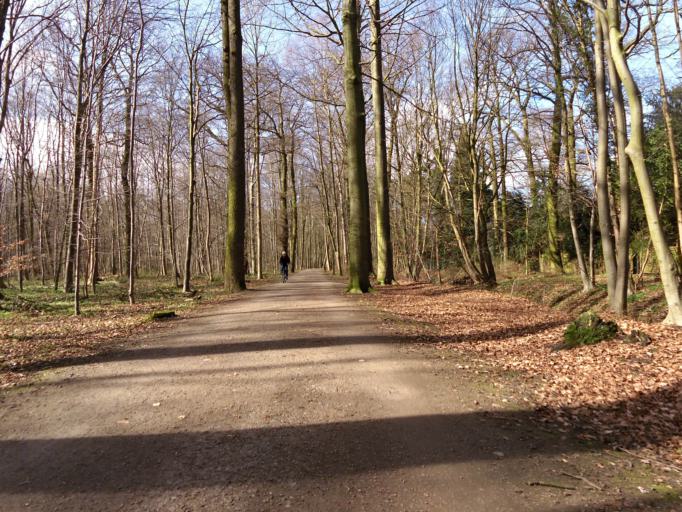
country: DE
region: Lower Saxony
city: Laatzen
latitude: 52.3685
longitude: 9.8000
